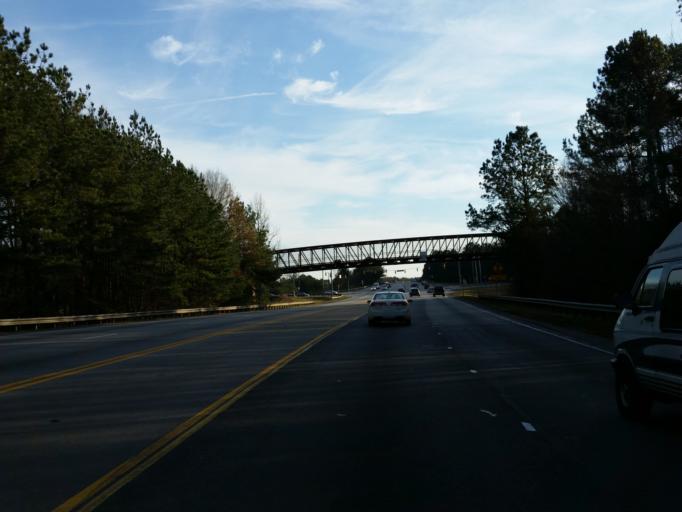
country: US
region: Georgia
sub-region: Cobb County
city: Powder Springs
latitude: 33.8697
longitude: -84.6969
